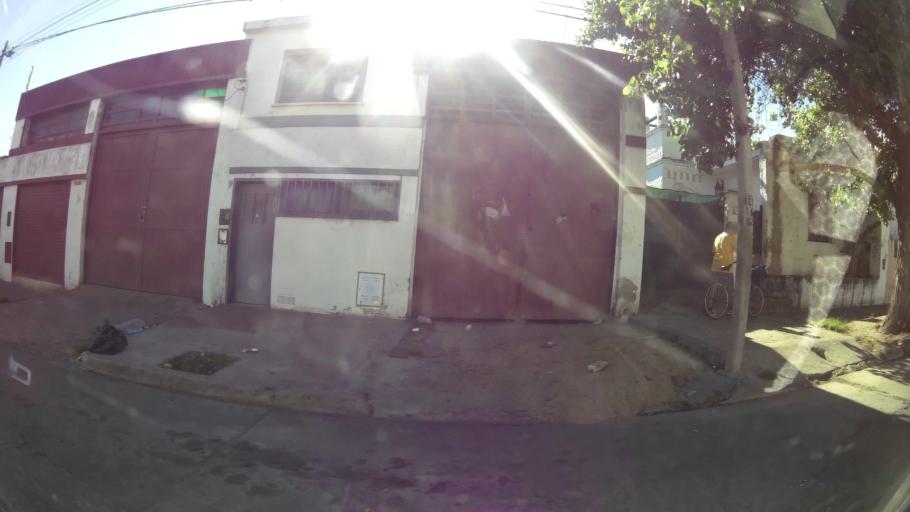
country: AR
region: Cordoba
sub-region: Departamento de Capital
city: Cordoba
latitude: -31.4259
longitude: -64.1623
